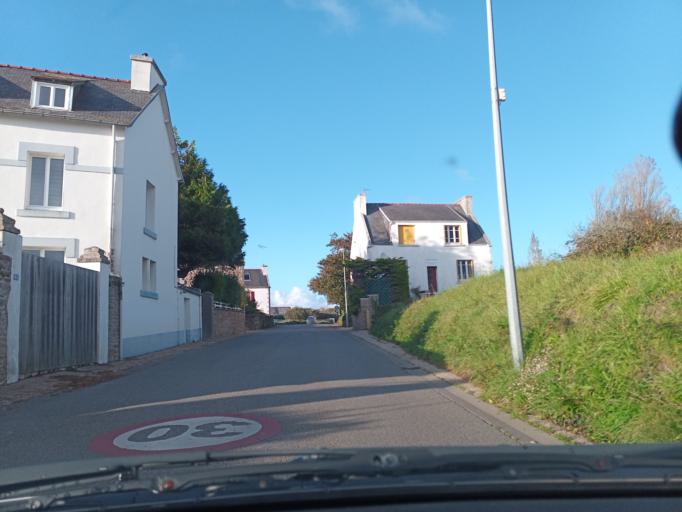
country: FR
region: Brittany
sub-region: Departement du Finistere
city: Esquibien
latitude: 48.0267
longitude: -4.5614
